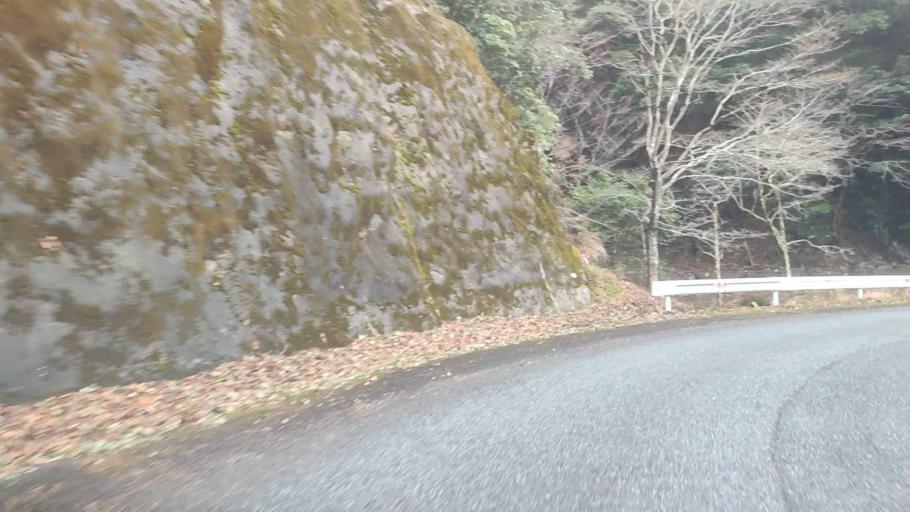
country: JP
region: Kumamoto
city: Matsubase
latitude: 32.4888
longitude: 130.9011
